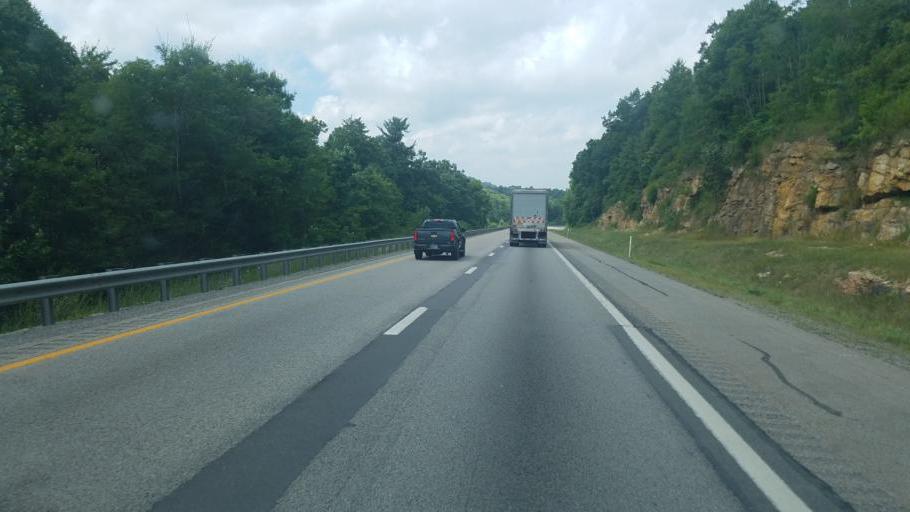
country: US
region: West Virginia
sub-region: Raleigh County
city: Shady Spring
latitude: 37.6596
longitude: -81.1128
